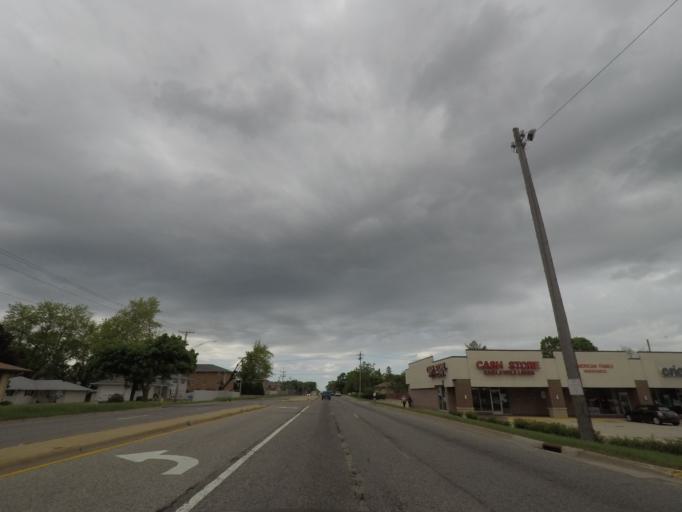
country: US
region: Illinois
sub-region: Winnebago County
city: Rockford
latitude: 42.2410
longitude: -89.0290
